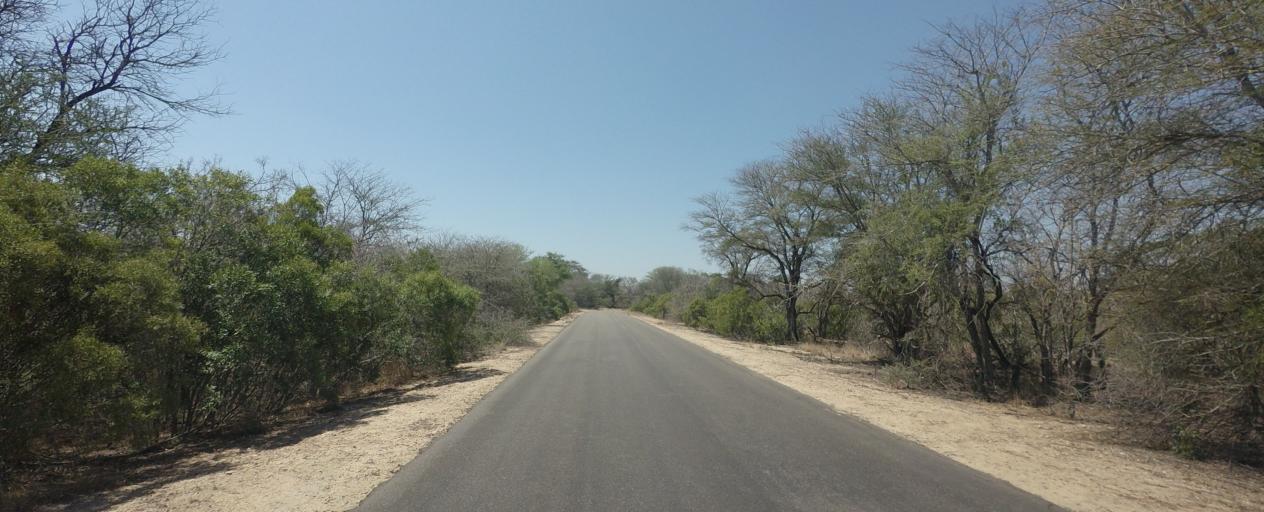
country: ZA
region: Limpopo
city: Thulamahashi
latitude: -24.4178
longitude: 31.5143
